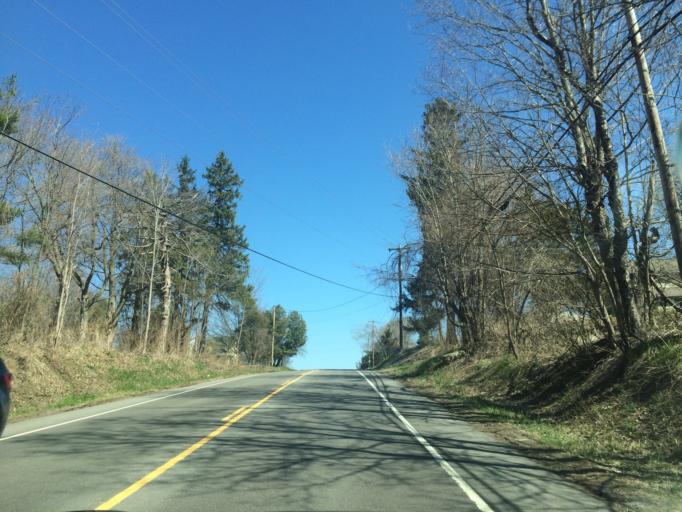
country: US
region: New York
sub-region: Wayne County
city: Macedon
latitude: 43.0861
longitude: -77.3016
